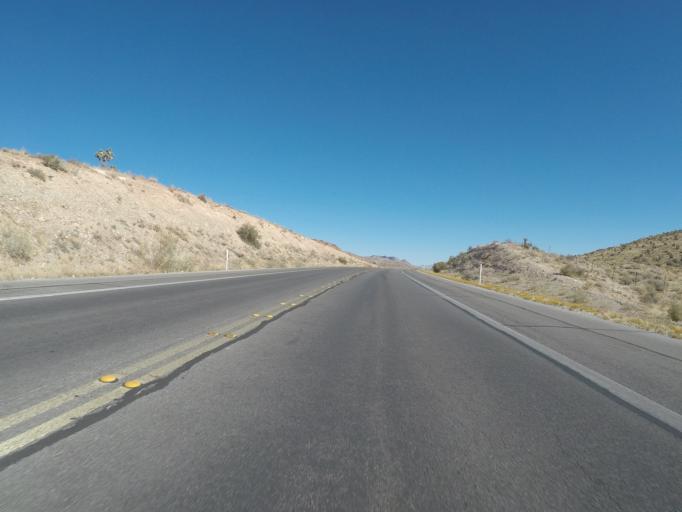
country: US
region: Nevada
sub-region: Clark County
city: Summerlin South
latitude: 36.1254
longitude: -115.4320
